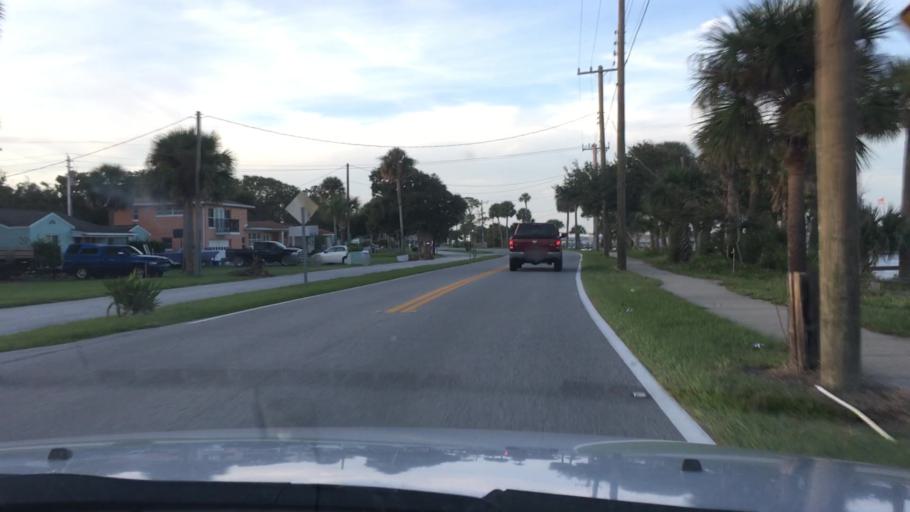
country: US
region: Florida
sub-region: Volusia County
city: Ormond Beach
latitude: 29.2695
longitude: -81.0473
